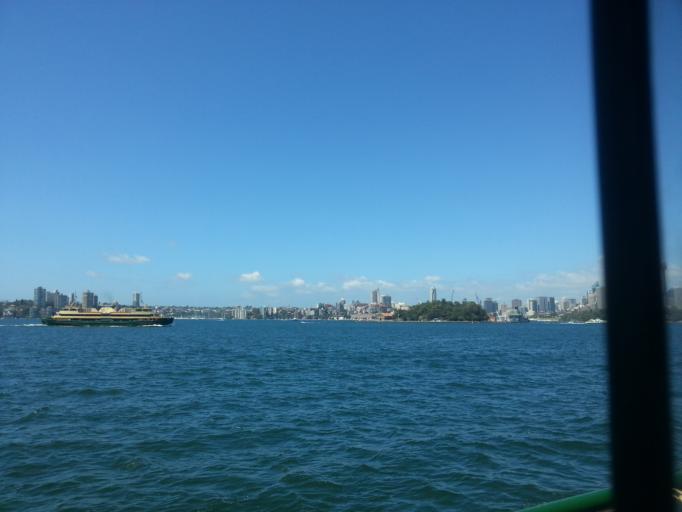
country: AU
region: New South Wales
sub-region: North Sydney
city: Cremorne Point
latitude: -33.8513
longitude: 151.2340
